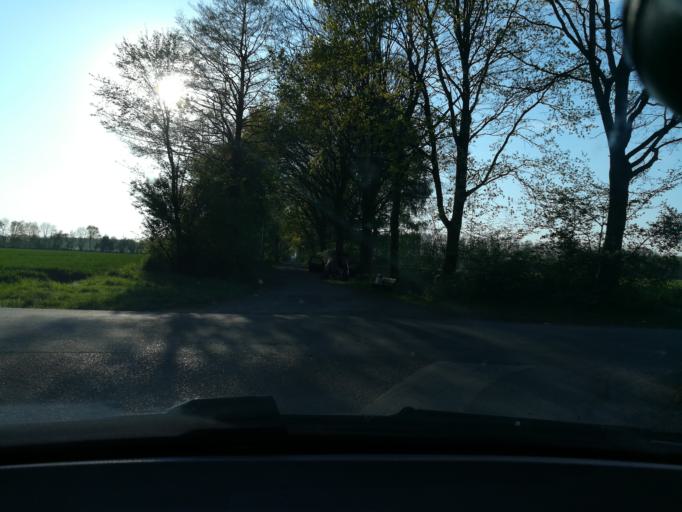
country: DE
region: North Rhine-Westphalia
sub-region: Regierungsbezirk Munster
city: Sassenberg
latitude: 52.0128
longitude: 8.0780
